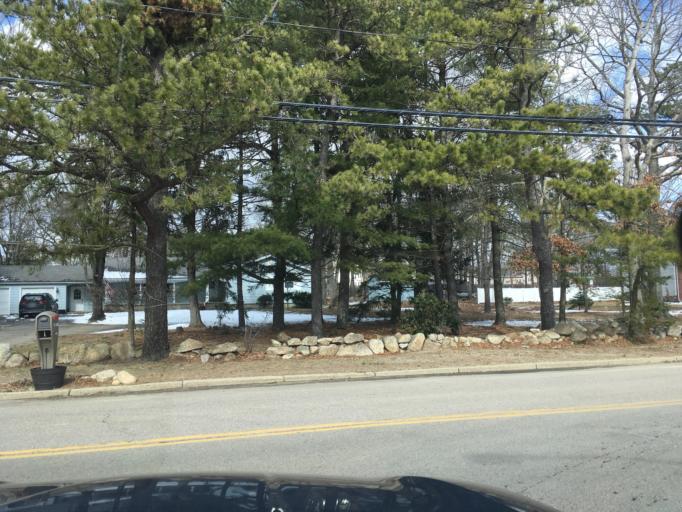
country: US
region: Rhode Island
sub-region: Kent County
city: West Warwick
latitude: 41.6858
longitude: -71.5924
